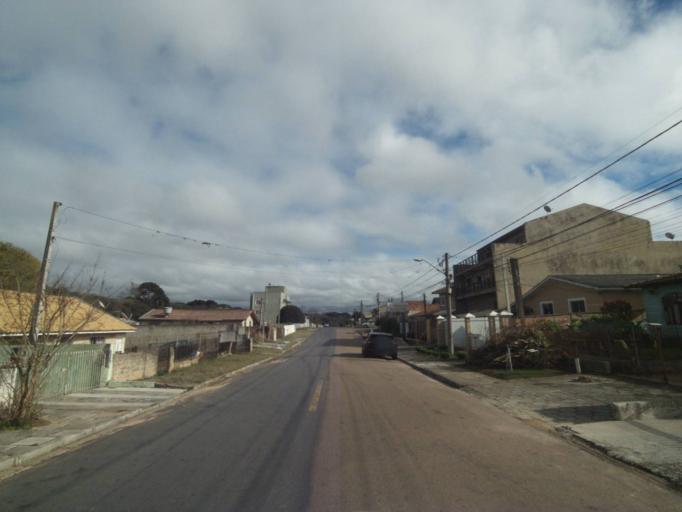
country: BR
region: Parana
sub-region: Sao Jose Dos Pinhais
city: Sao Jose dos Pinhais
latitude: -25.5212
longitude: -49.3068
